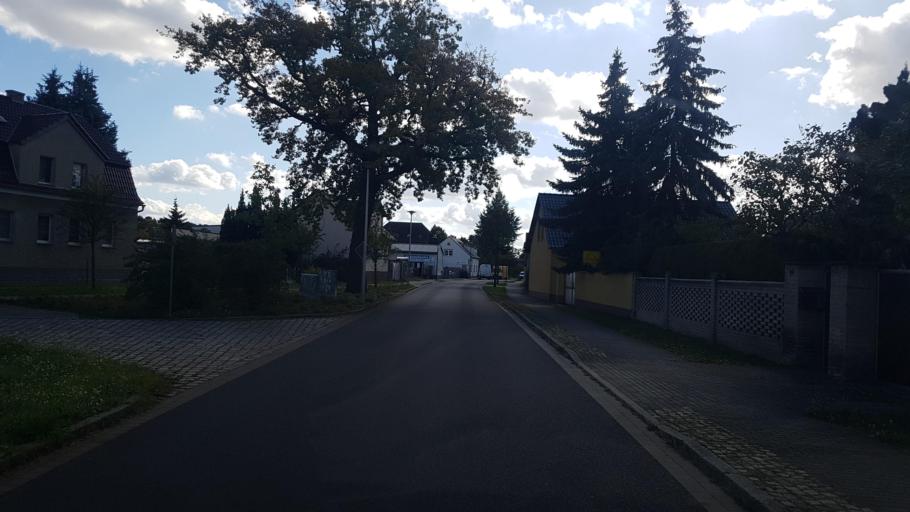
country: DE
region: Brandenburg
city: Cottbus
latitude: 51.7839
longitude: 14.3355
